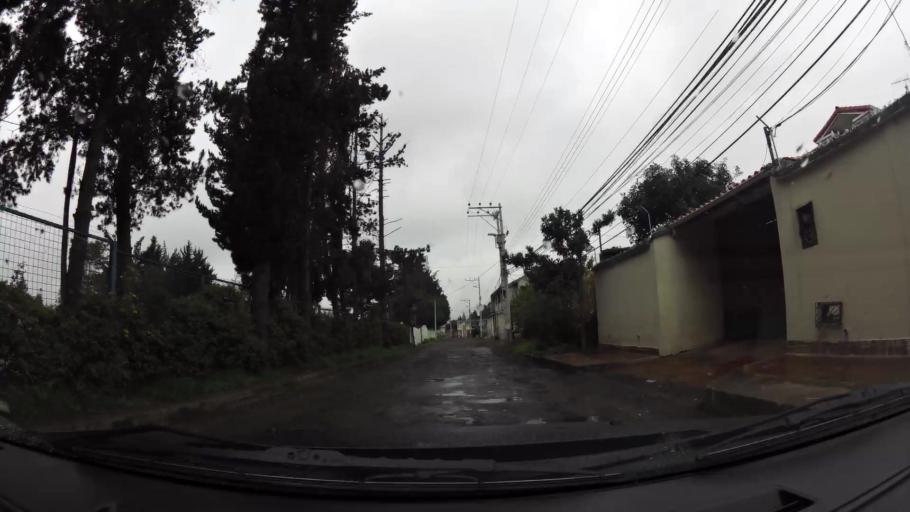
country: EC
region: Pichincha
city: Sangolqui
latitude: -0.2731
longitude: -78.4564
